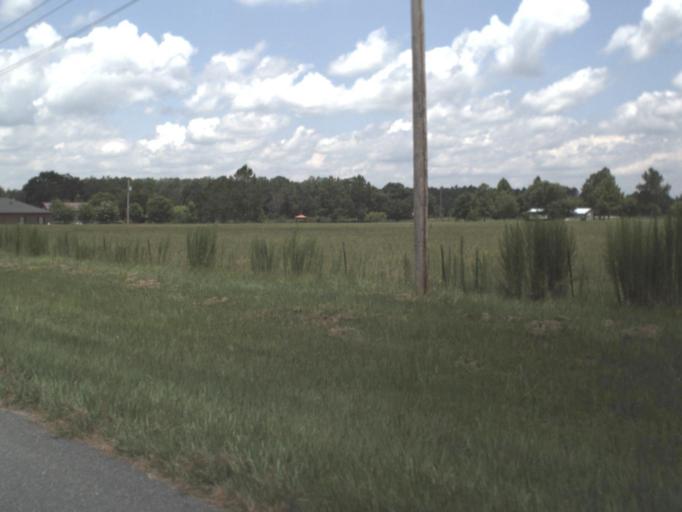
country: US
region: Florida
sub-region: Union County
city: Lake Butler
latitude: 30.0104
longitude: -82.4484
